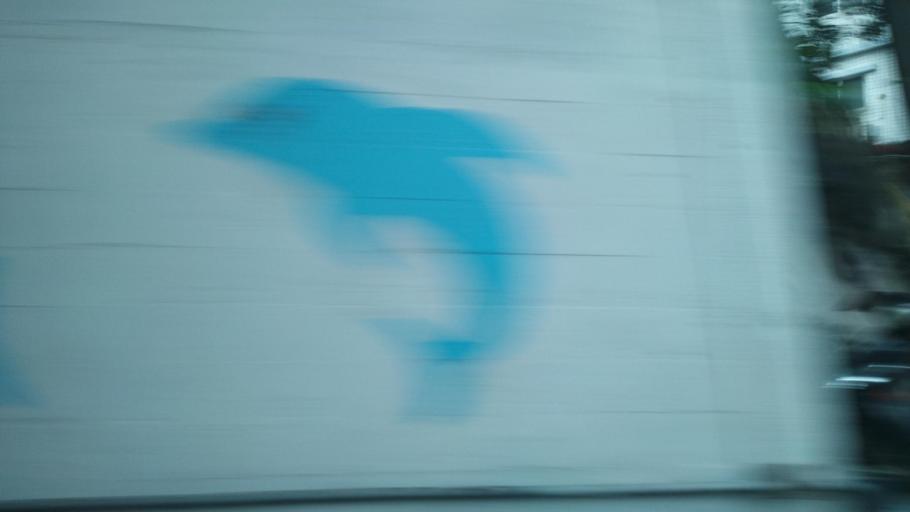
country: TW
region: Taiwan
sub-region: Keelung
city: Keelung
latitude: 25.2063
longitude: 121.6858
